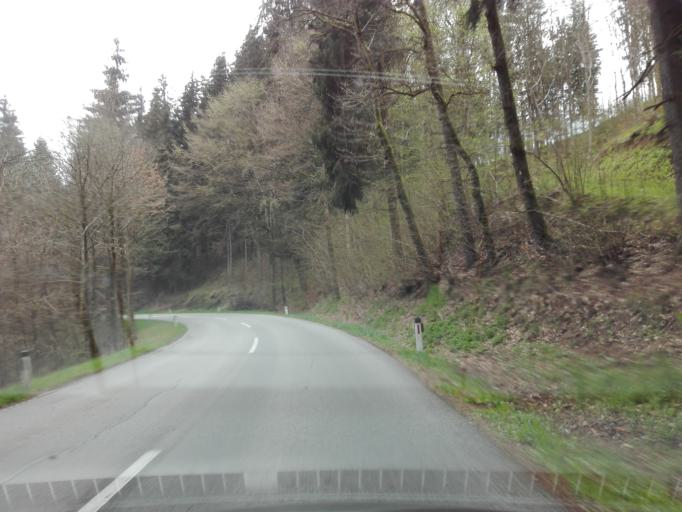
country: AT
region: Upper Austria
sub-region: Politischer Bezirk Rohrbach
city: Atzesberg
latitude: 48.5401
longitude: 13.9521
